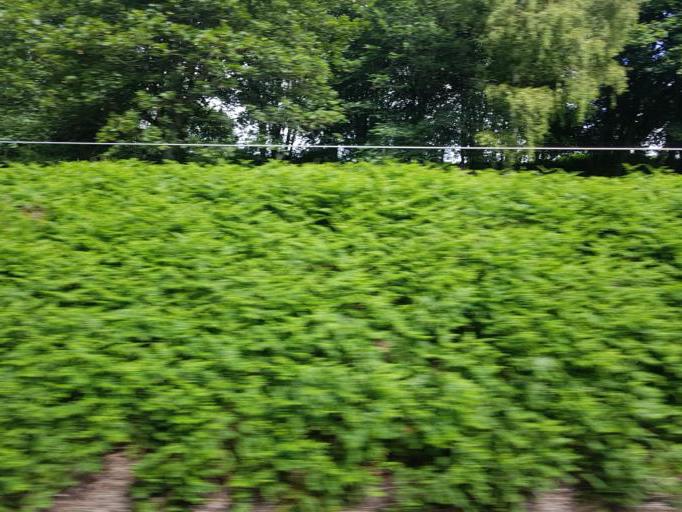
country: GB
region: Scotland
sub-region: Falkirk
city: Polmont
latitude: 55.9797
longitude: -3.6762
